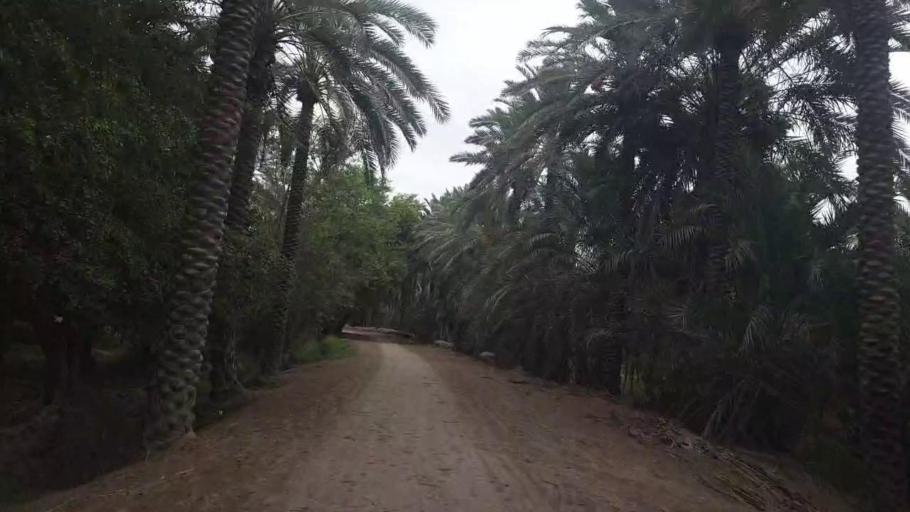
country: PK
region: Sindh
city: Khairpur
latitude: 27.5821
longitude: 68.7489
